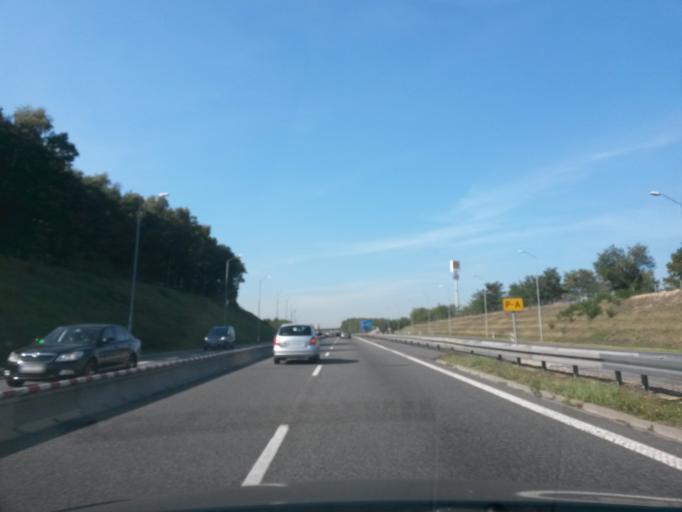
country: PL
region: Silesian Voivodeship
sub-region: Ruda Slaska
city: Ruda Slaska
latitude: 50.2496
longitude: 18.8870
